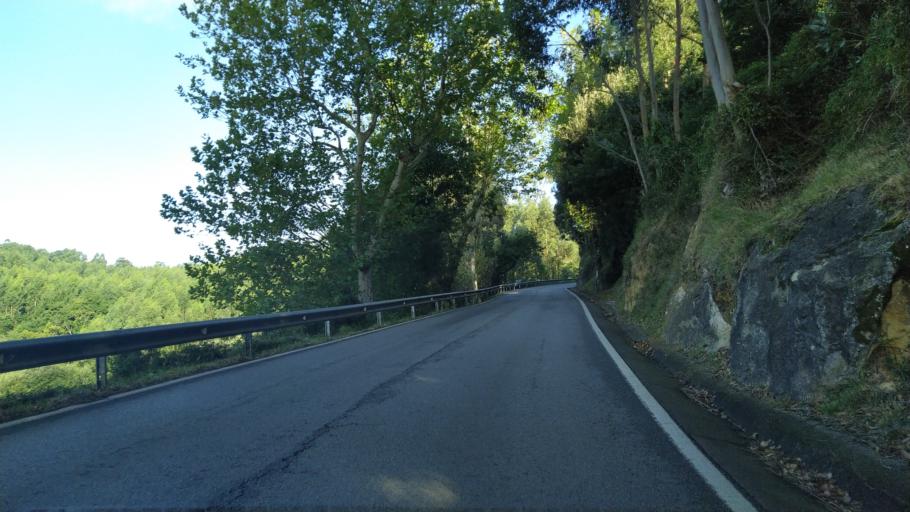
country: ES
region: Cantabria
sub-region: Provincia de Cantabria
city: Santa Cruz de Bezana
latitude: 43.4496
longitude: -3.9277
